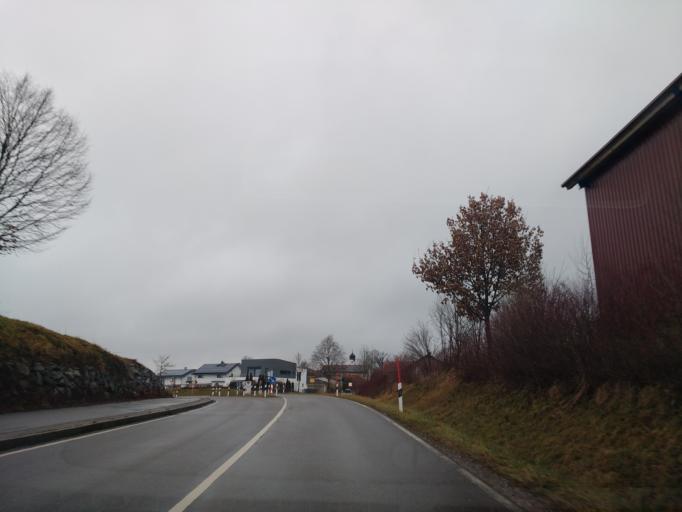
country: DE
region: Bavaria
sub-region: Swabia
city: Neuburg
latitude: 47.7757
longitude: 10.3606
